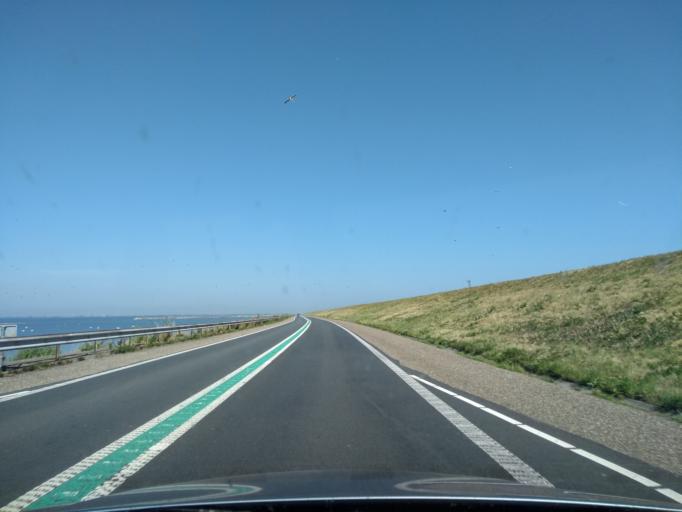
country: NL
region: North Holland
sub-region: Gemeente Enkhuizen
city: Enkhuizen
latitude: 52.6498
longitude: 5.3981
